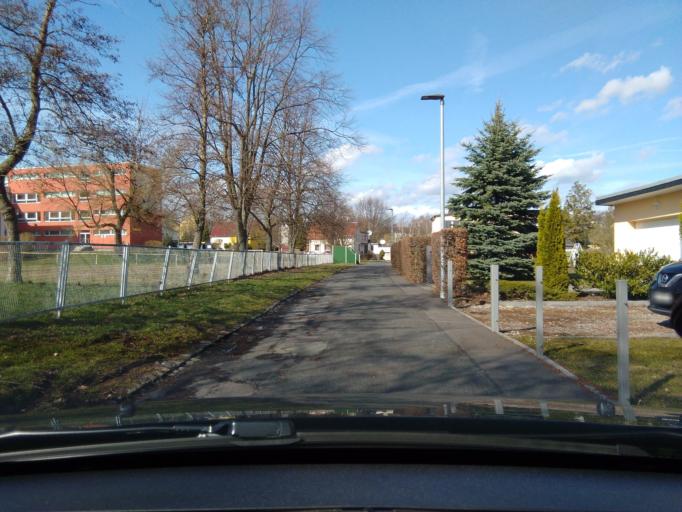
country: DE
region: Saxony
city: Wittgensdorf
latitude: 50.8382
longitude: 12.8744
